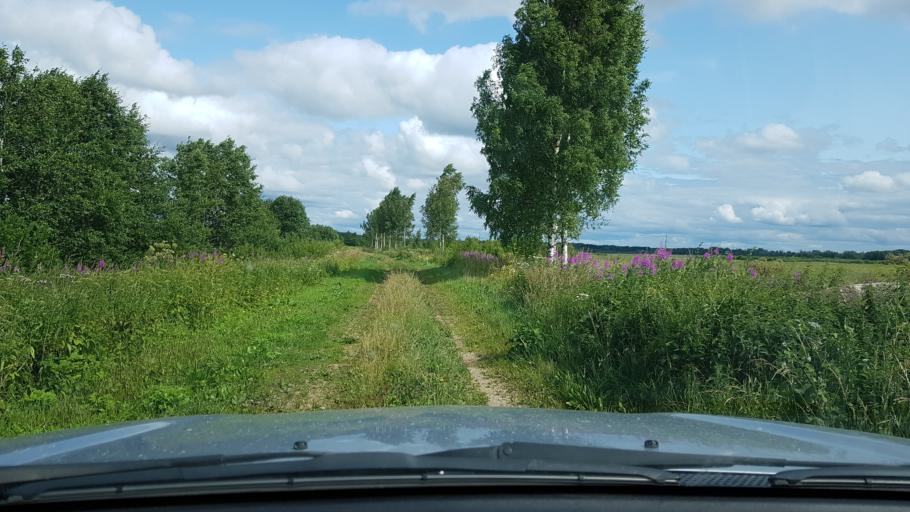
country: EE
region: Ida-Virumaa
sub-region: Narva-Joesuu linn
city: Narva-Joesuu
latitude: 59.3858
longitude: 27.9250
